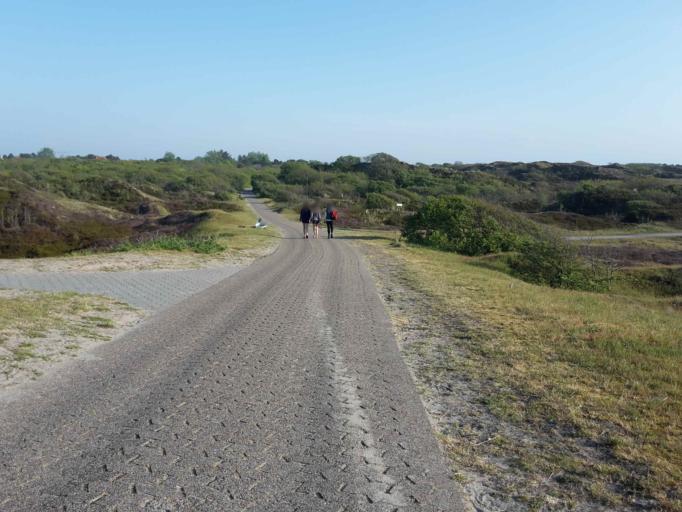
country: DE
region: Lower Saxony
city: Spiekeroog
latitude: 53.7763
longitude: 7.6983
